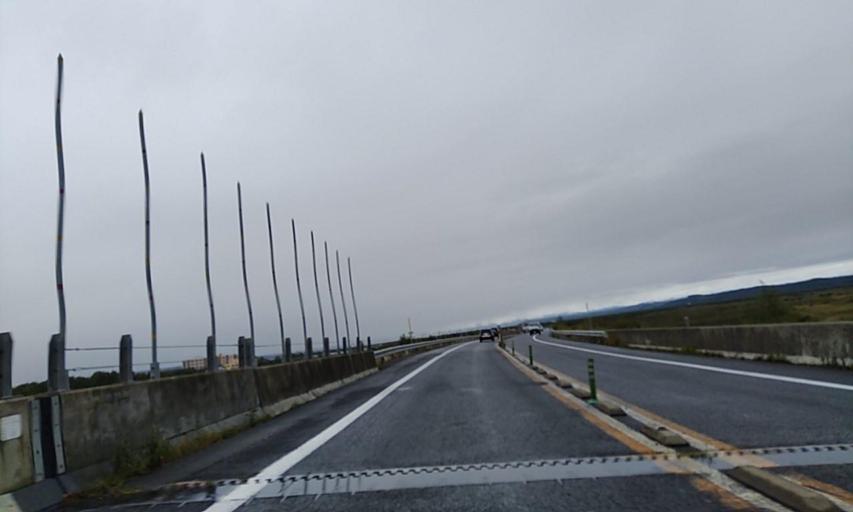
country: JP
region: Hokkaido
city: Kushiro
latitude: 43.0348
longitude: 144.3654
